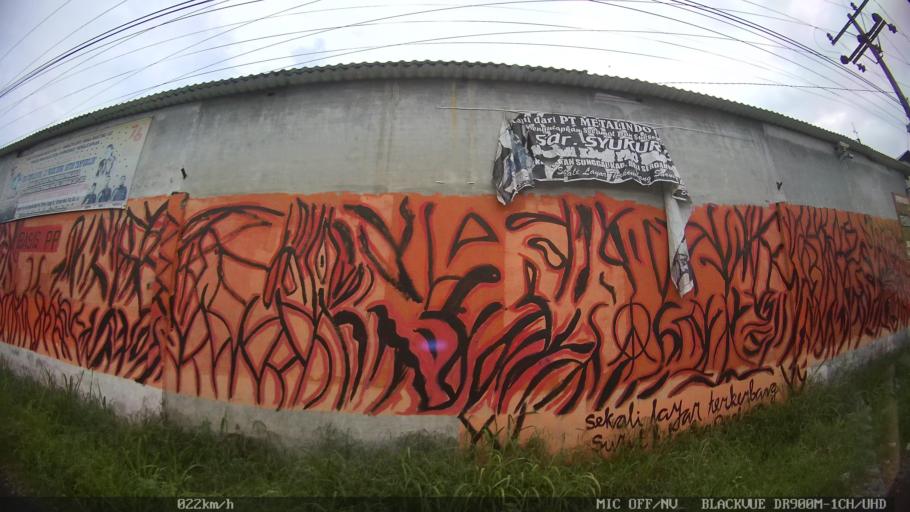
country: ID
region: North Sumatra
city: Sunggal
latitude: 3.6145
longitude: 98.5862
